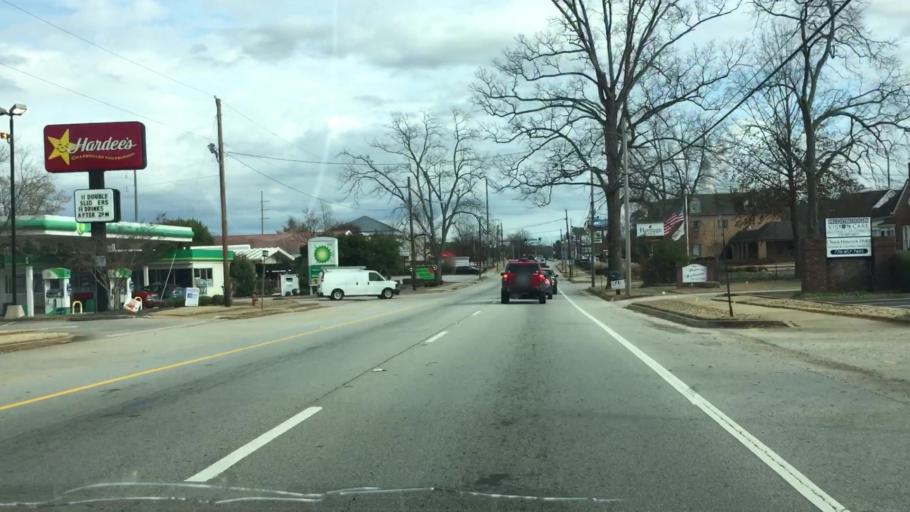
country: US
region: Georgia
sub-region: Henry County
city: McDonough
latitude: 33.4469
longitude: -84.1414
